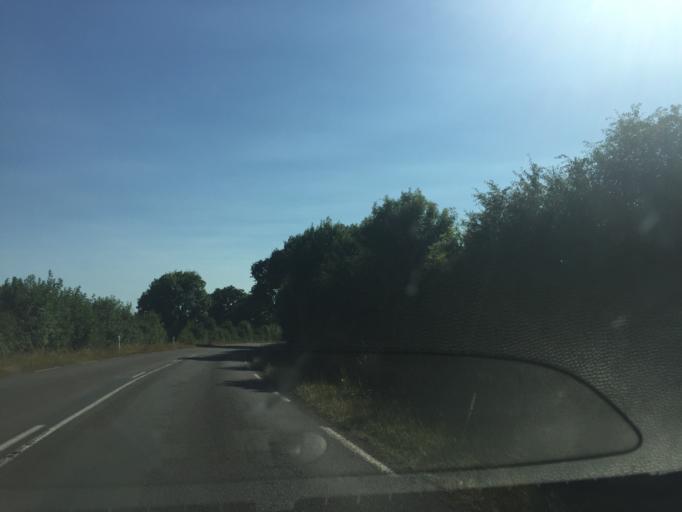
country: FR
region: Poitou-Charentes
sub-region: Departement des Deux-Sevres
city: Melle
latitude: 46.2414
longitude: -0.1044
